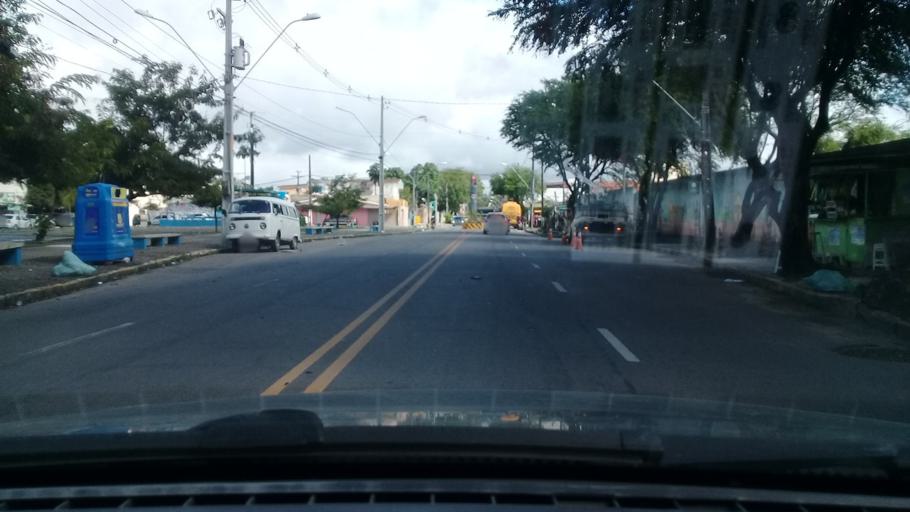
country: BR
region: Pernambuco
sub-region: Recife
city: Recife
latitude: -8.0666
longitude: -34.9277
